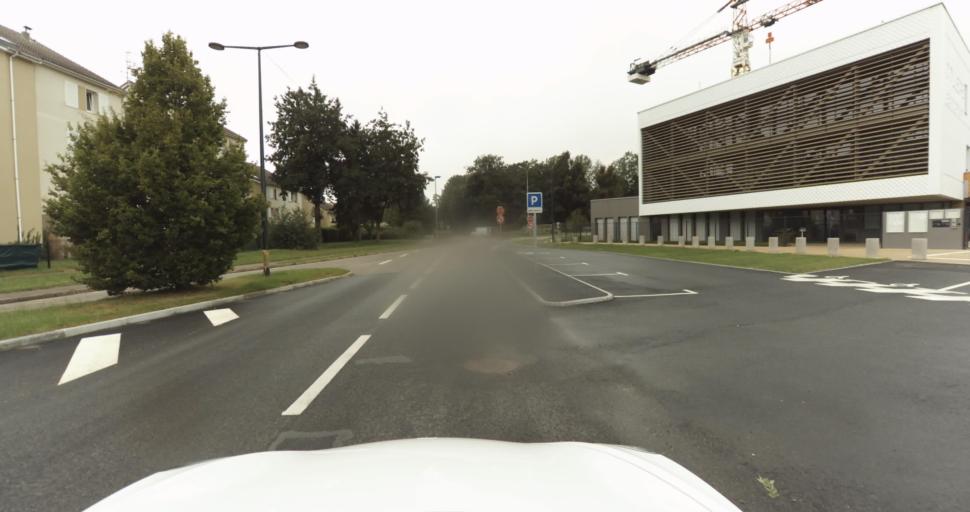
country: FR
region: Haute-Normandie
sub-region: Departement de l'Eure
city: Aviron
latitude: 49.0392
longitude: 1.1299
